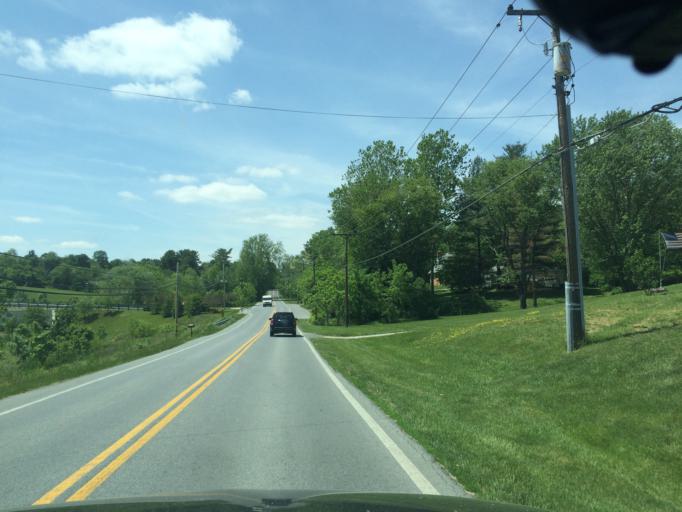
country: US
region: Maryland
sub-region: Carroll County
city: Westminster
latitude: 39.5521
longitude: -76.9579
